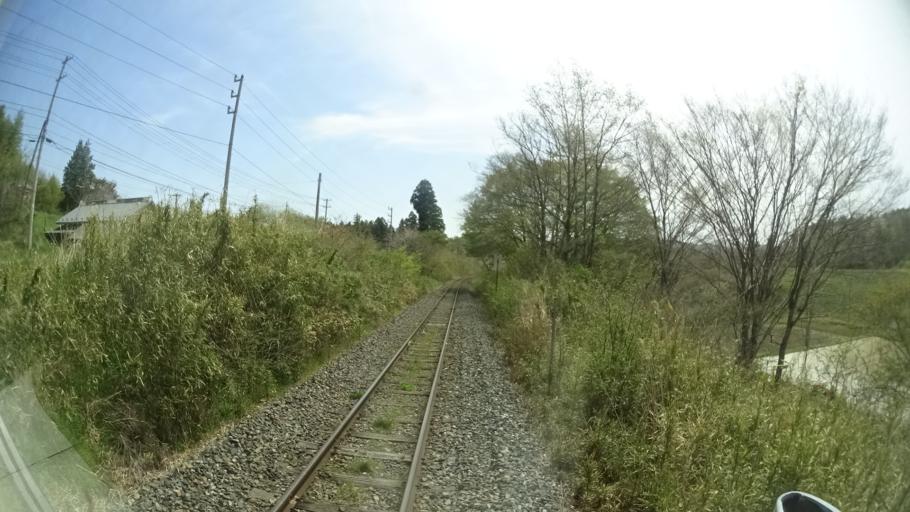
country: JP
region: Iwate
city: Ichinoseki
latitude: 38.9963
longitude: 141.2744
